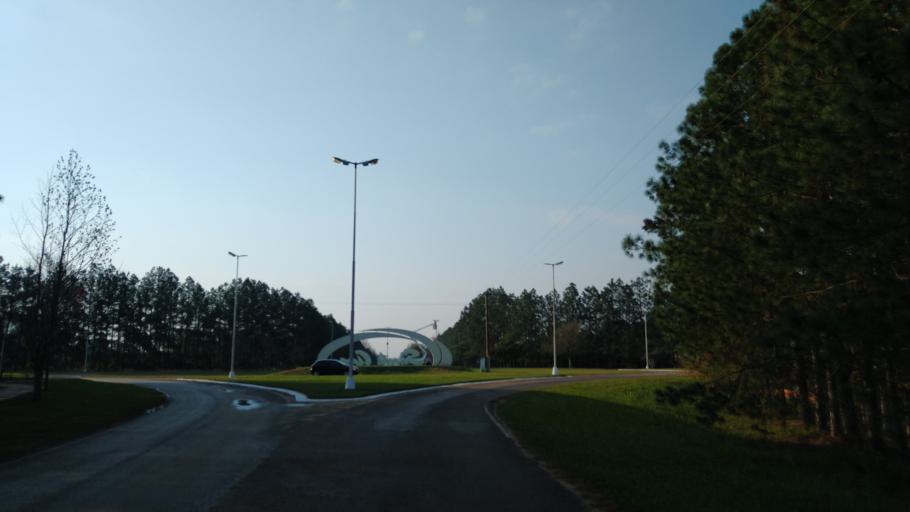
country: AR
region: Entre Rios
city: Santa Ana
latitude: -30.9009
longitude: -57.9243
